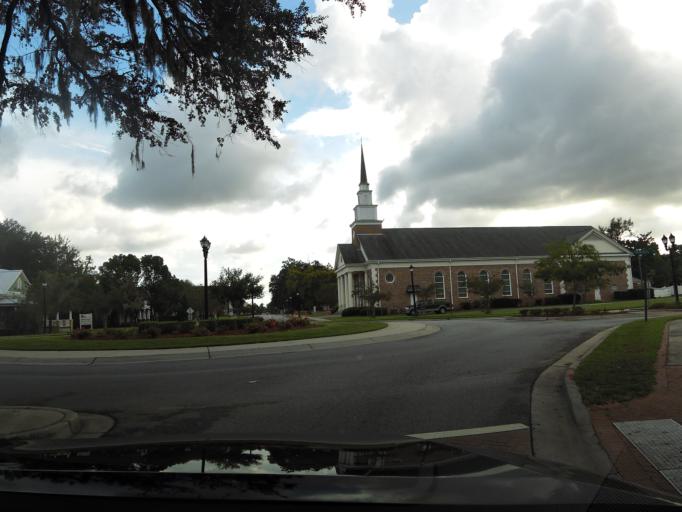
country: US
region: Georgia
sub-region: Liberty County
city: Hinesville
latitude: 31.8501
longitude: -81.5957
